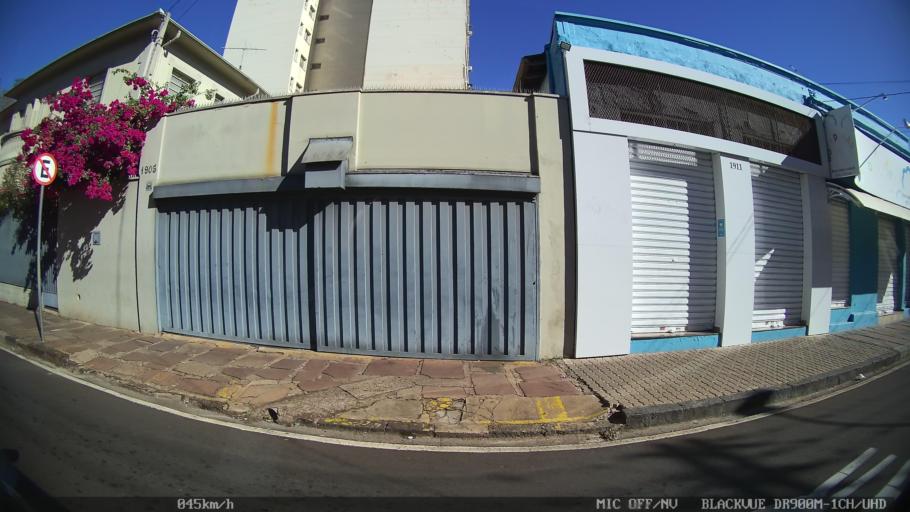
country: BR
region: Sao Paulo
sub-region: Franca
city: Franca
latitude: -20.5371
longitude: -47.3987
